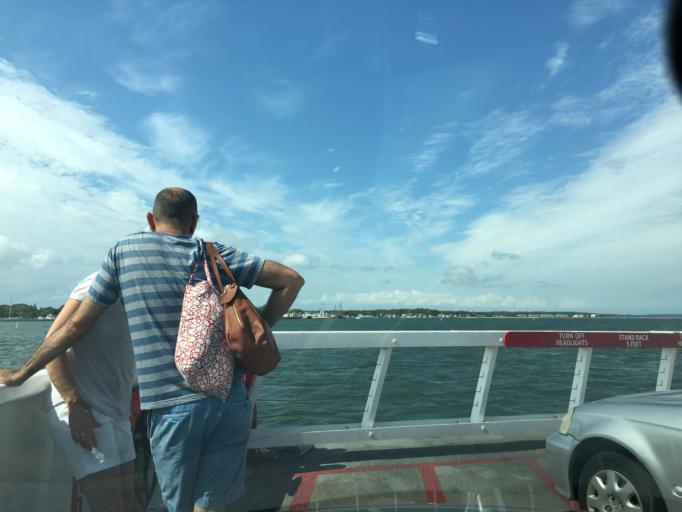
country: US
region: New York
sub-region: Suffolk County
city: Greenport
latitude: 41.0951
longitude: -72.3581
